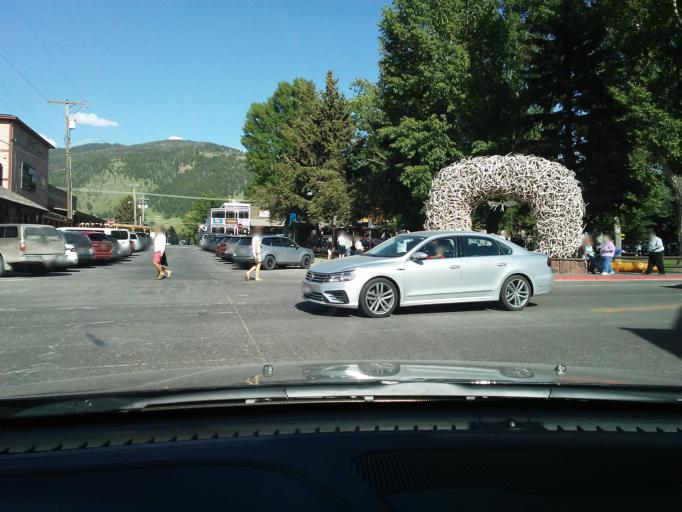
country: US
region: Wyoming
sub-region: Teton County
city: Jackson
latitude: 43.4802
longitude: -110.7625
